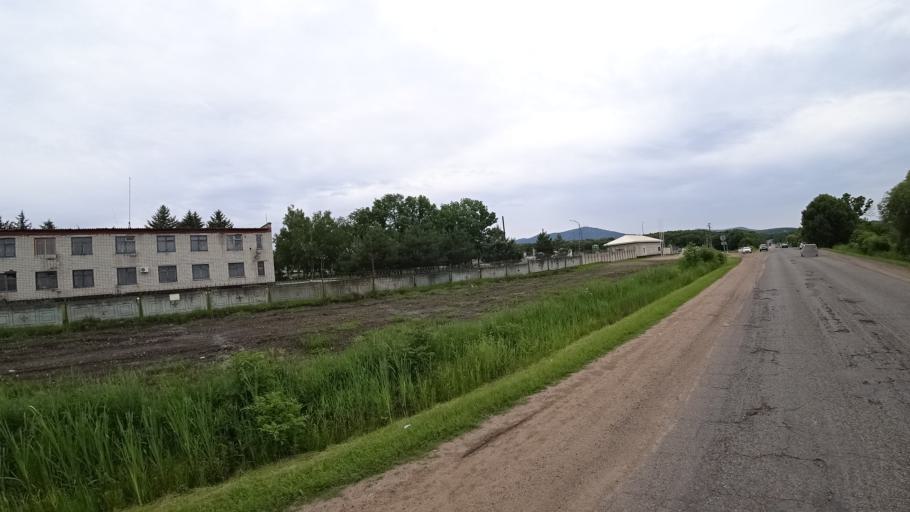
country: RU
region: Primorskiy
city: Novosysoyevka
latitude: 44.1810
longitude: 133.3495
